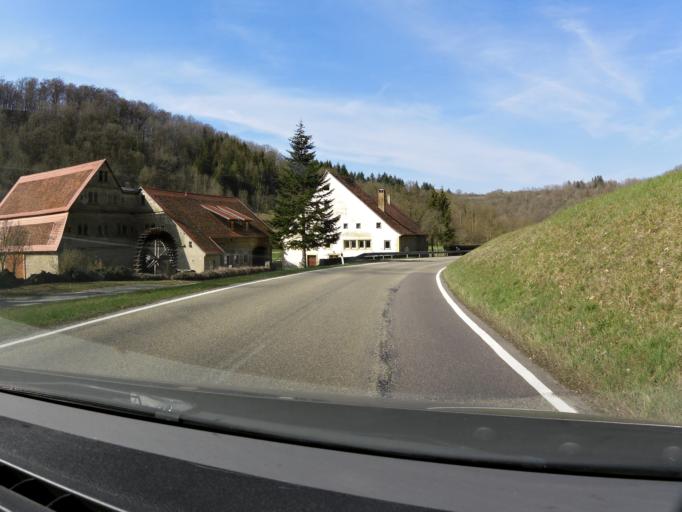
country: DE
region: Bavaria
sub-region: Regierungsbezirk Mittelfranken
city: Rothenburg ob der Tauber
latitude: 49.3915
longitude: 10.1660
